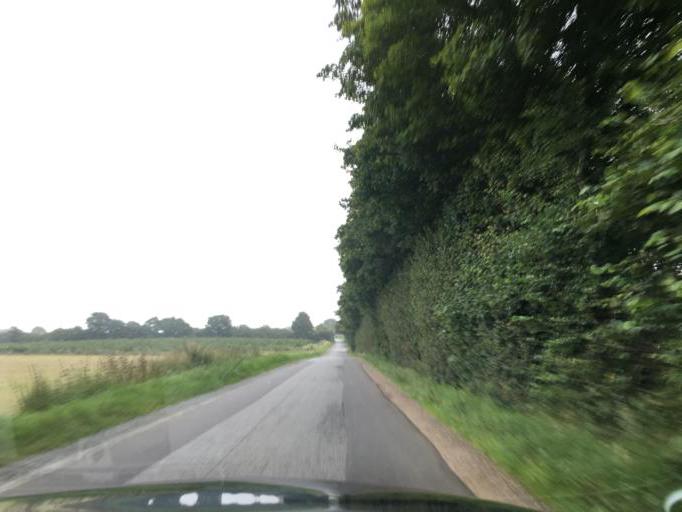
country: DK
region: South Denmark
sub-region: Kolding Kommune
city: Kolding
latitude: 55.5661
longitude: 9.4708
